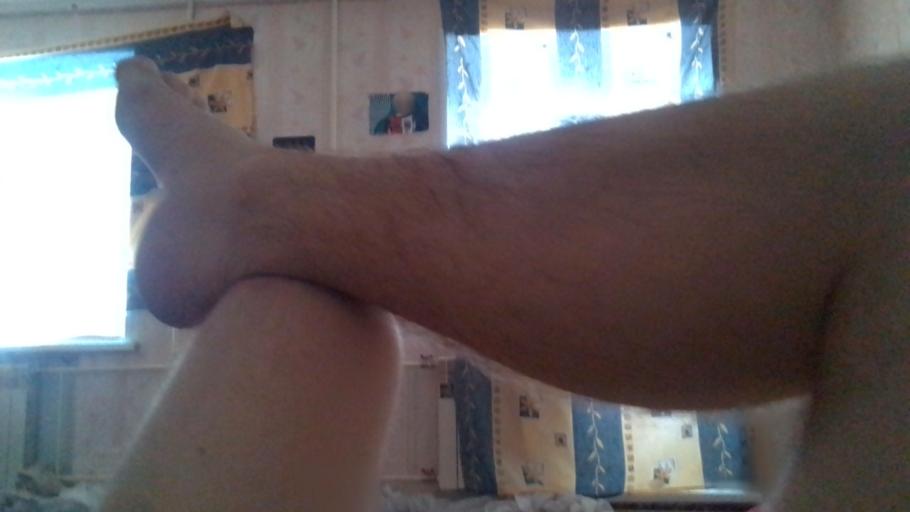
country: RU
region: Tomsk
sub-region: Tomskiy Rayon
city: Tomsk
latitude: 56.4768
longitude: 84.9931
